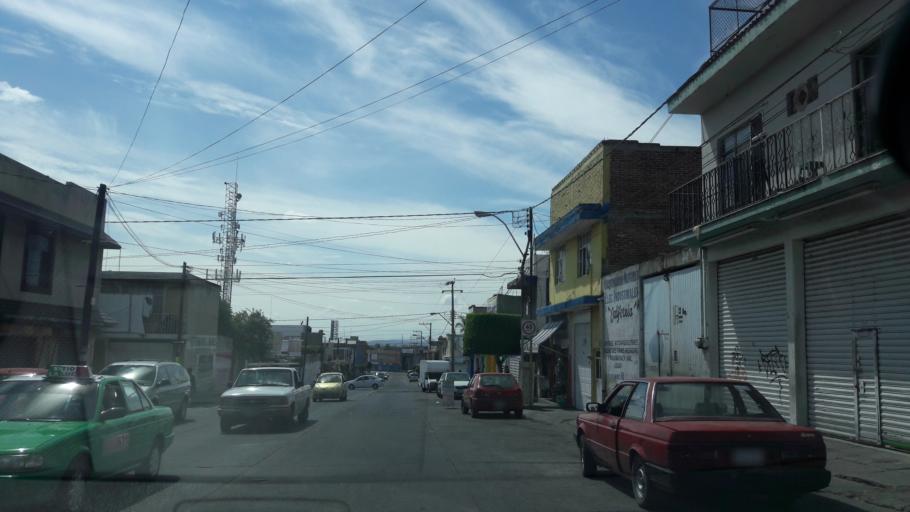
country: MX
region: Guanajuato
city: Leon
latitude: 21.1088
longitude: -101.6997
